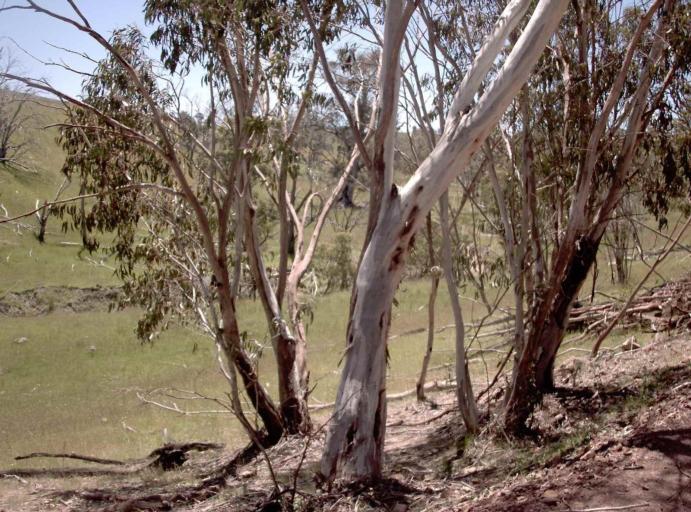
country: AU
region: New South Wales
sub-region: Snowy River
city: Jindabyne
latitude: -37.0618
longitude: 148.2982
